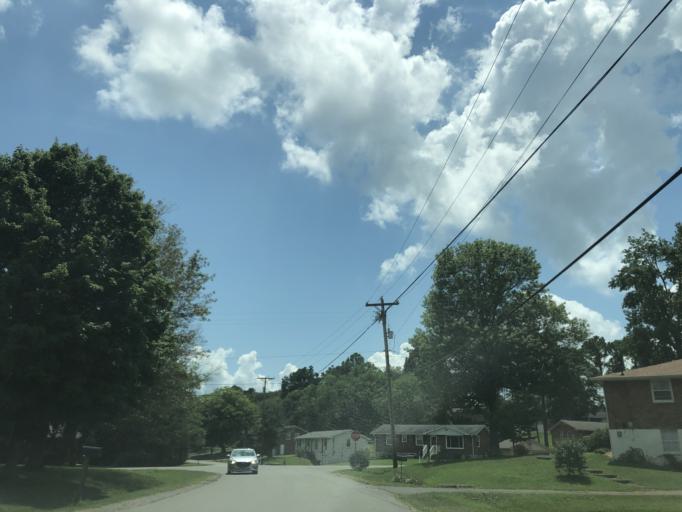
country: US
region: Tennessee
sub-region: Davidson County
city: Lakewood
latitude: 36.2010
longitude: -86.6243
